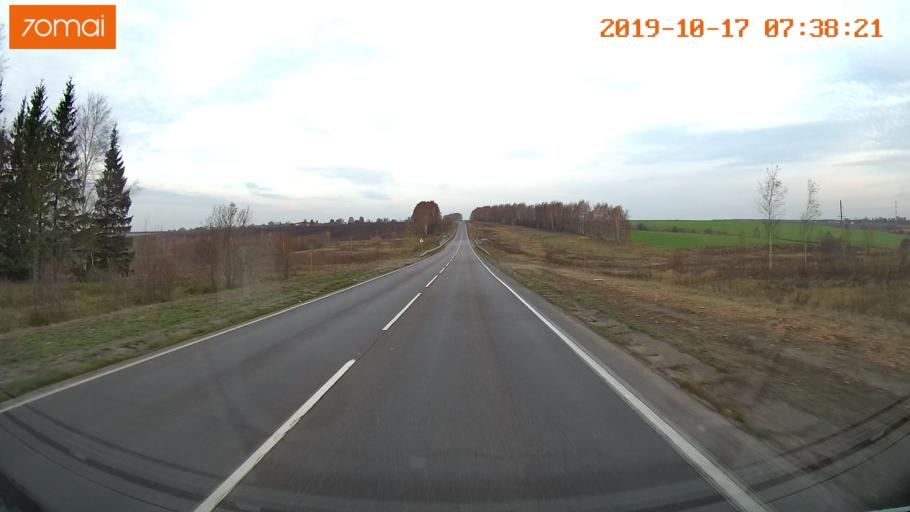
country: RU
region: Vladimir
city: Yur'yev-Pol'skiy
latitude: 56.4549
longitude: 39.8768
